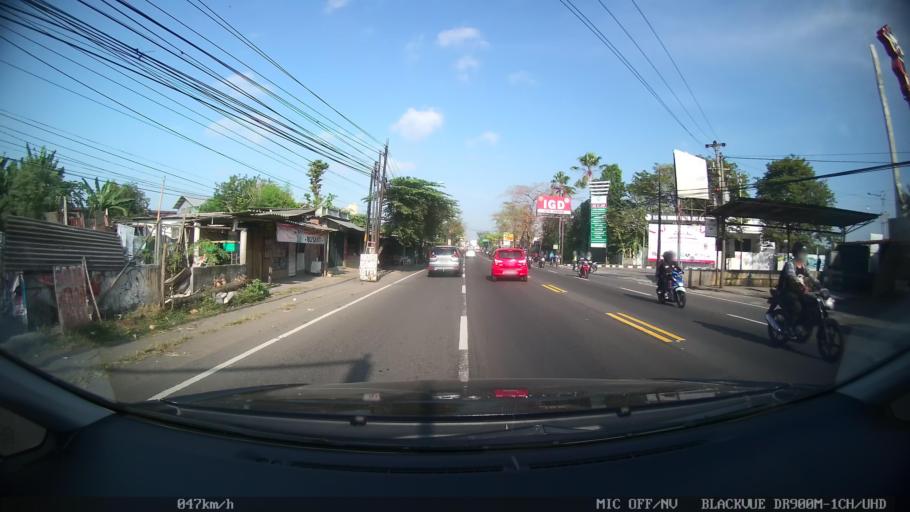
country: ID
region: Daerah Istimewa Yogyakarta
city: Gamping Lor
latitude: -7.8012
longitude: 110.3184
